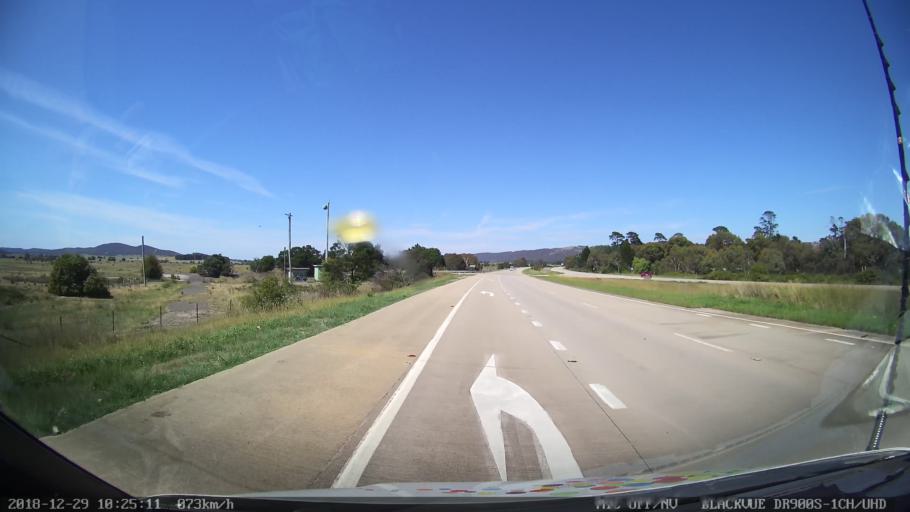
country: AU
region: New South Wales
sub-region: Yass Valley
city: Gundaroo
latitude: -34.9170
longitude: 149.4380
